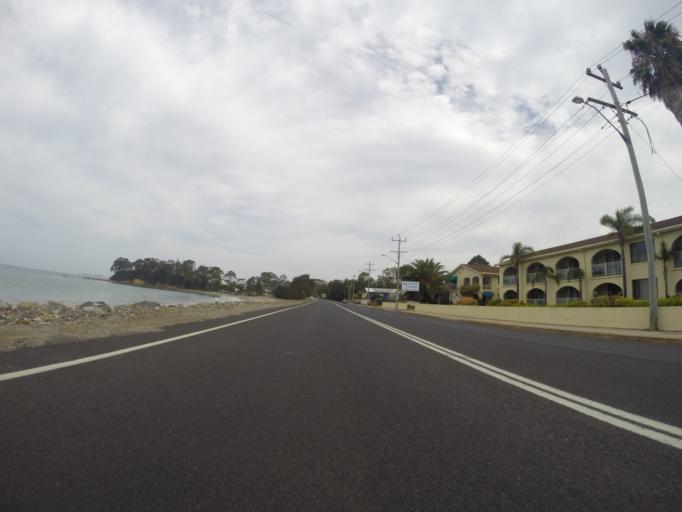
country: AU
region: New South Wales
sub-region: Eurobodalla
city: Batemans Bay
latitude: -35.7357
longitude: 150.2073
